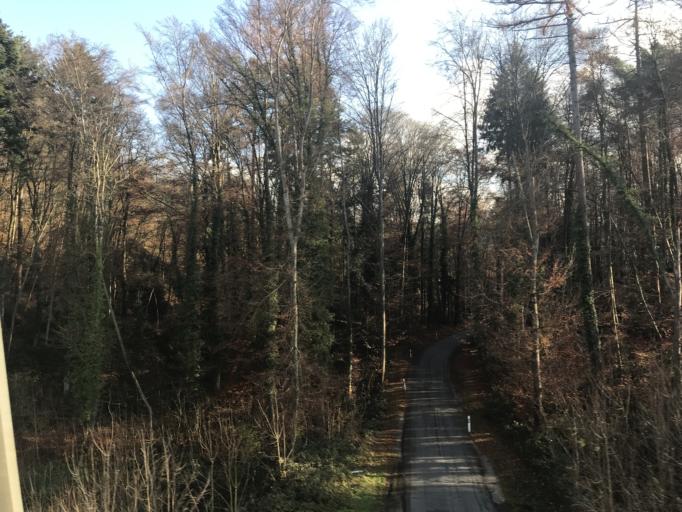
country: CH
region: Schaffhausen
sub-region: Bezirk Schaffhausen
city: Neuhausen
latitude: 47.6758
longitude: 8.6063
